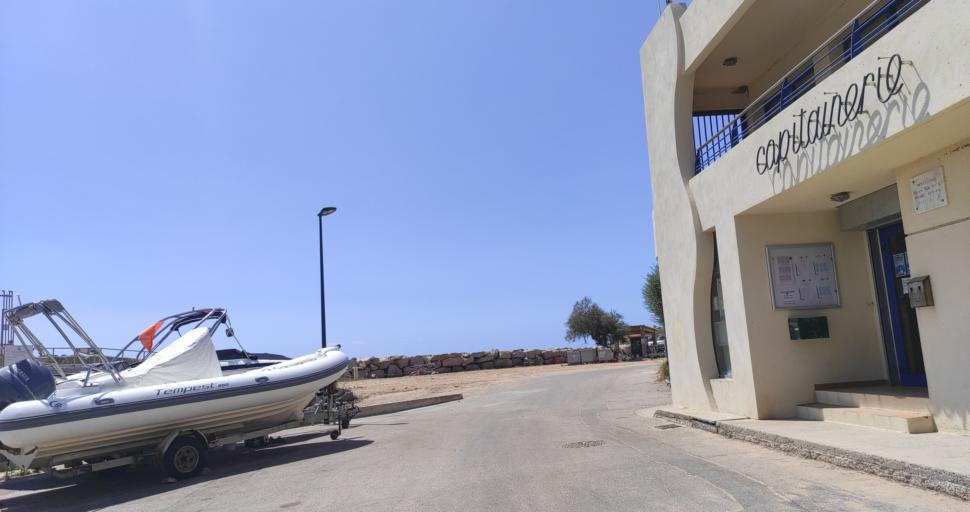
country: FR
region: Corsica
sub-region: Departement de la Corse-du-Sud
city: Cargese
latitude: 42.1304
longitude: 8.5961
